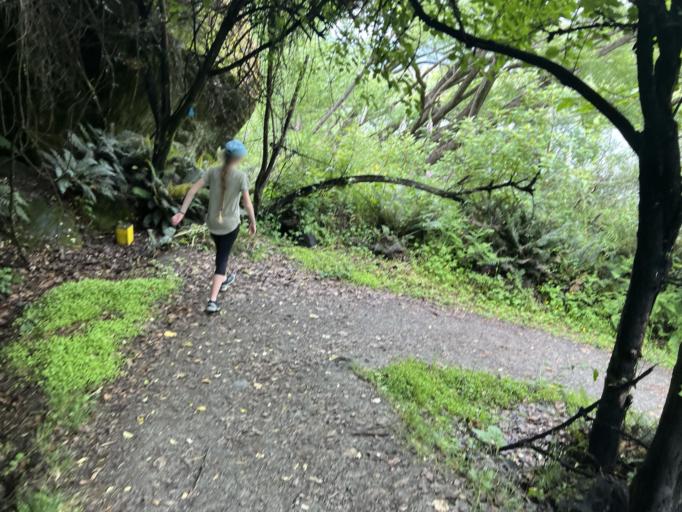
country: NZ
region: Otago
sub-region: Queenstown-Lakes District
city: Wanaka
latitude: -44.6465
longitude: 168.9630
